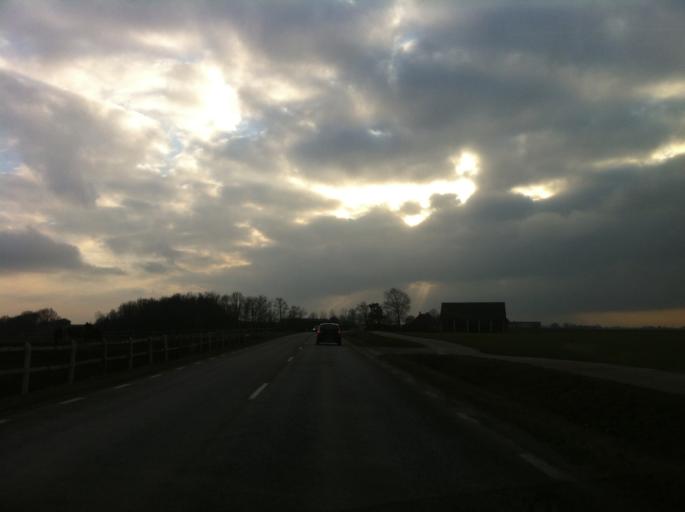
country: SE
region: Skane
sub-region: Kavlinge Kommun
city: Kaevlinge
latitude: 55.7843
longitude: 13.0760
